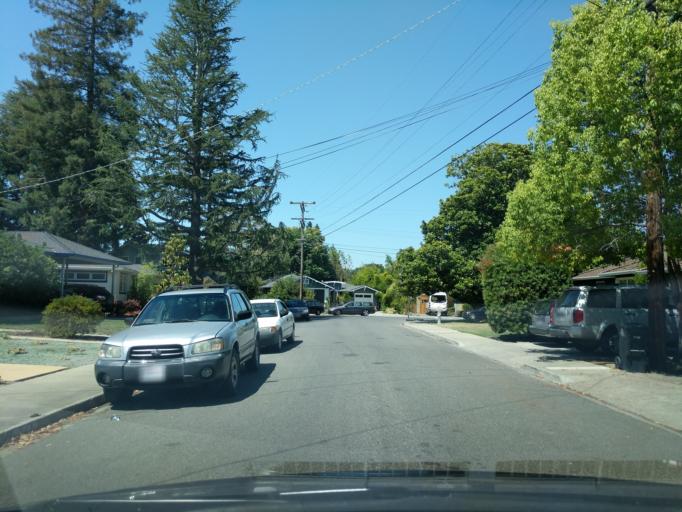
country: US
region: California
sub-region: Santa Clara County
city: Mountain View
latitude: 37.3875
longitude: -122.0760
